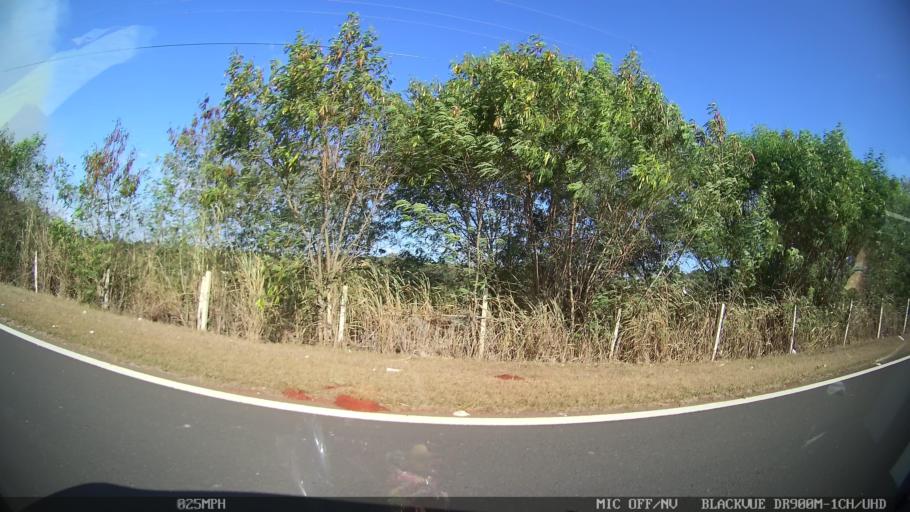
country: BR
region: Sao Paulo
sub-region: Piracicaba
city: Piracicaba
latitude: -22.7008
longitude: -47.6017
